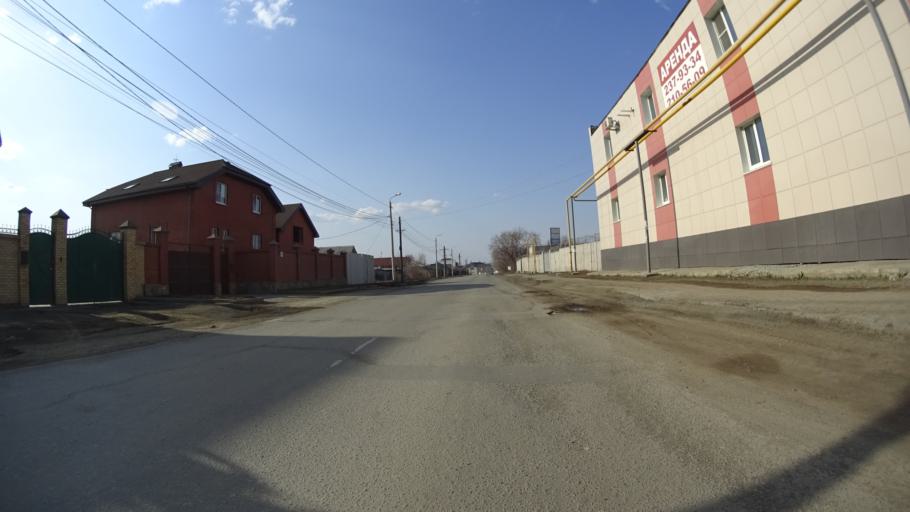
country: RU
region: Chelyabinsk
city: Novosineglazovskiy
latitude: 55.1086
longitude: 61.3343
